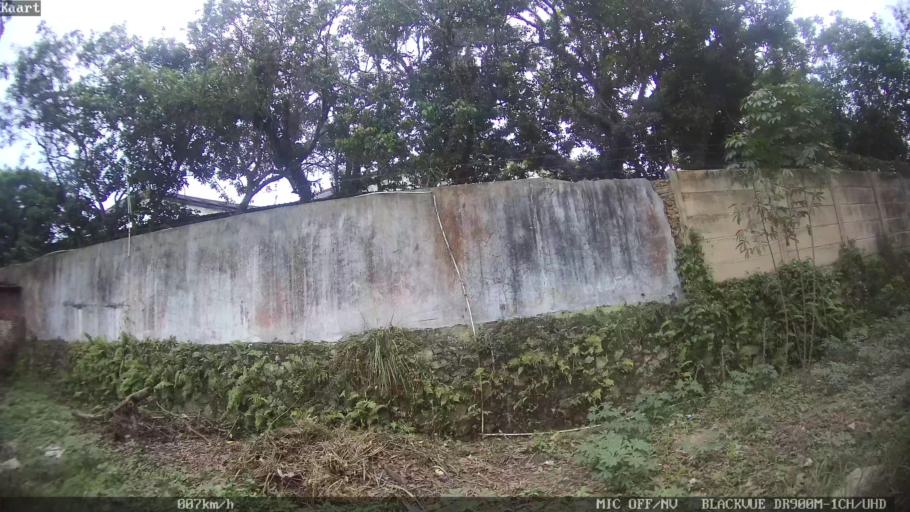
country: ID
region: Lampung
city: Panjang
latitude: -5.4360
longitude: 105.3251
